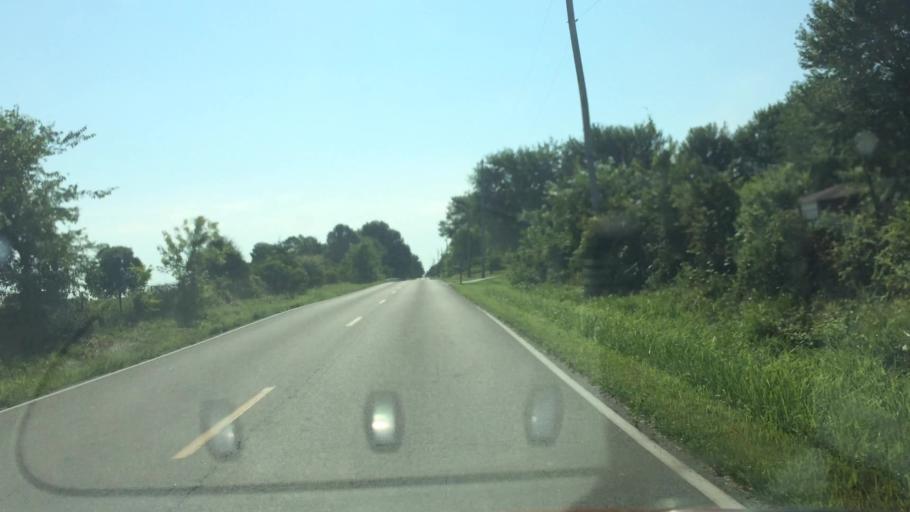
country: US
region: Missouri
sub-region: Greene County
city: Strafford
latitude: 37.2558
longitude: -93.1804
